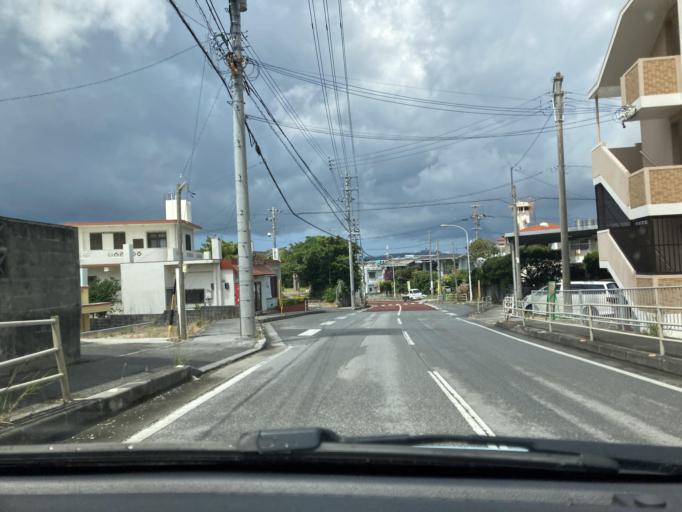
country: JP
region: Okinawa
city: Tomigusuku
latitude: 26.1799
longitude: 127.7429
